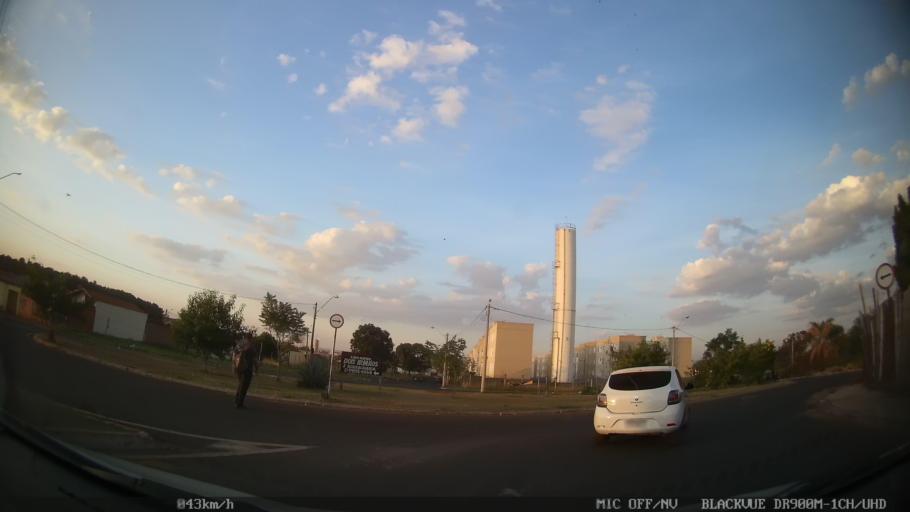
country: BR
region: Sao Paulo
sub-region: Ribeirao Preto
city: Ribeirao Preto
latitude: -21.1221
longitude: -47.8240
